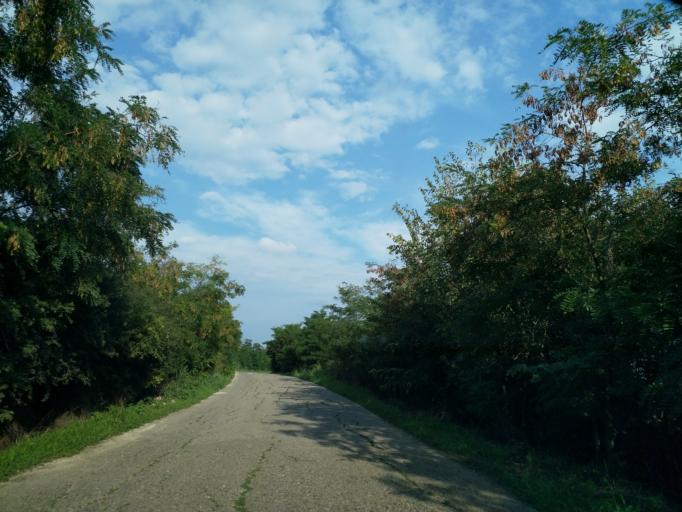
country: RS
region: Central Serbia
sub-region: Pomoravski Okrug
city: Jagodina
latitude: 43.9923
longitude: 21.2019
